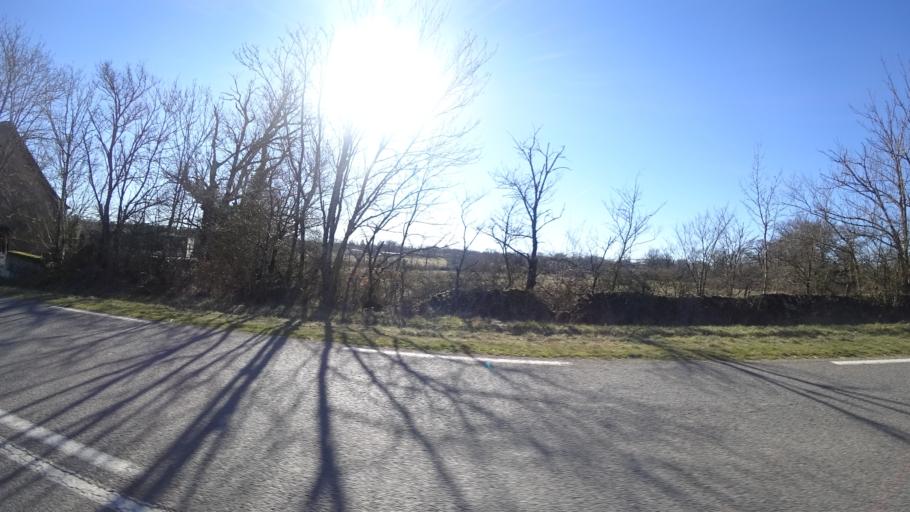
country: FR
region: Midi-Pyrenees
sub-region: Departement de l'Aveyron
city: Sebazac-Concoures
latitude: 44.3988
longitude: 2.5609
